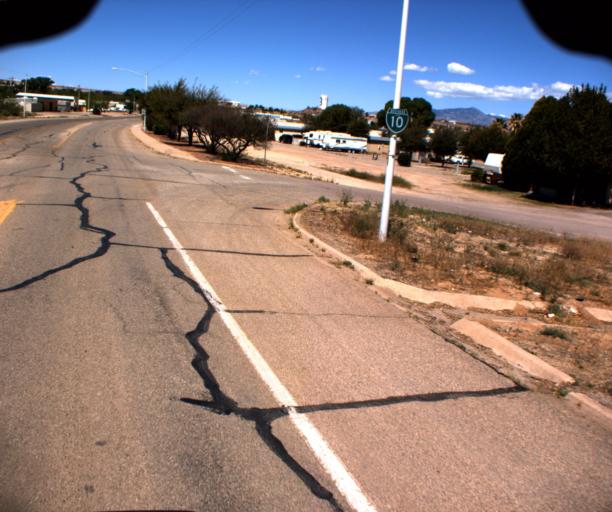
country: US
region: Arizona
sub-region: Cochise County
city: Benson
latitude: 31.9651
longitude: -110.2819
